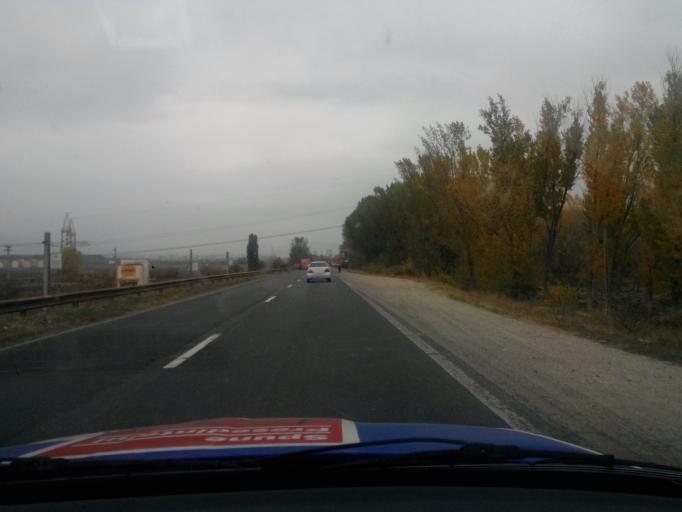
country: RO
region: Galati
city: Galati
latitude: 45.3764
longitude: 28.0175
